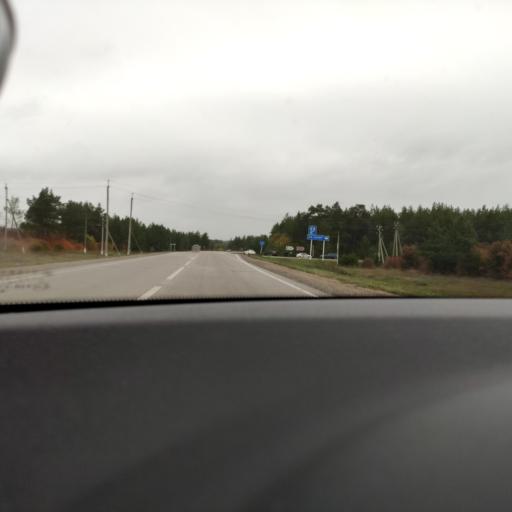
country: RU
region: Samara
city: Mirnyy
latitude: 53.5279
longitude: 50.3099
